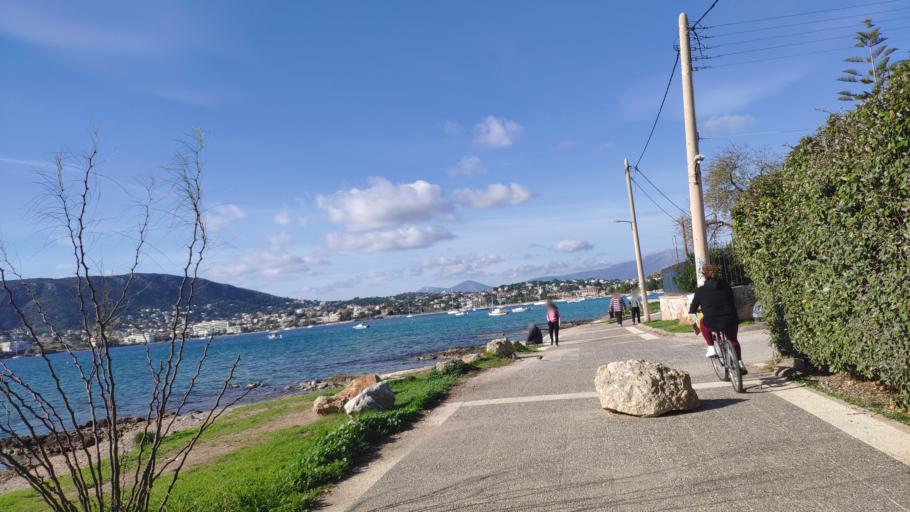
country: GR
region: Attica
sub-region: Nomarchia Anatolikis Attikis
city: Limin Mesoyaias
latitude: 37.8915
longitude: 24.0213
